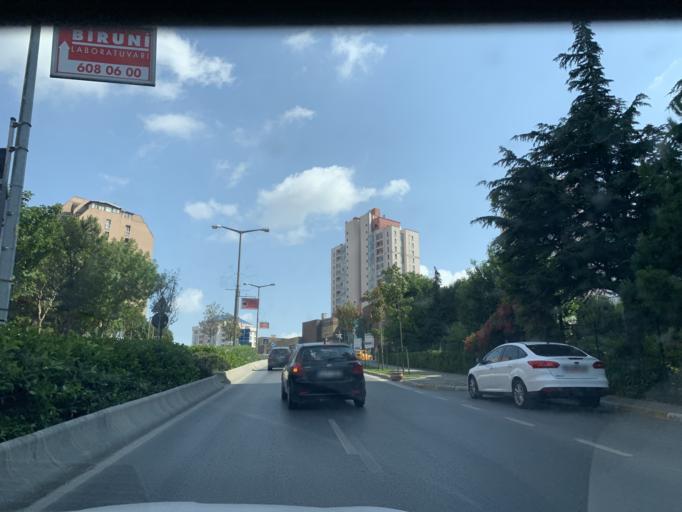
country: TR
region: Istanbul
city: Esenyurt
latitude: 41.0650
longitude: 28.6850
